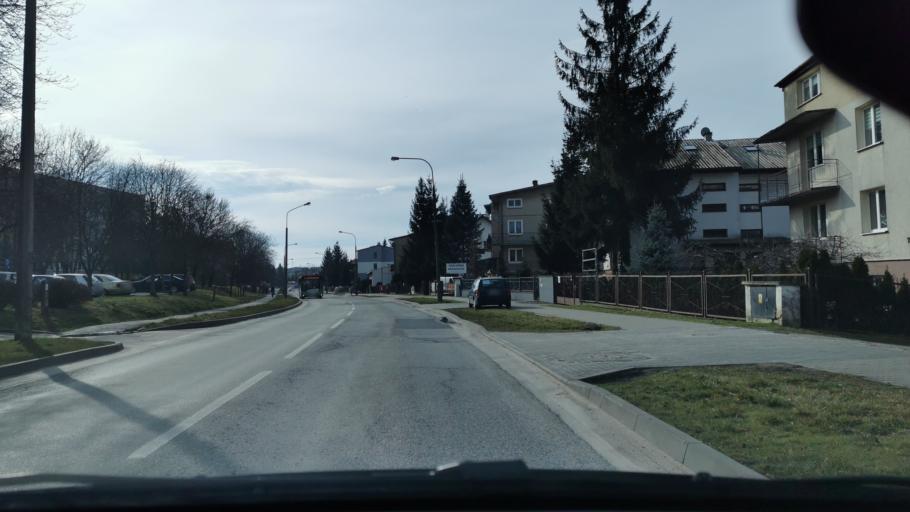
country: PL
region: Lublin Voivodeship
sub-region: Powiat lubelski
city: Lublin
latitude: 51.2079
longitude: 22.5415
